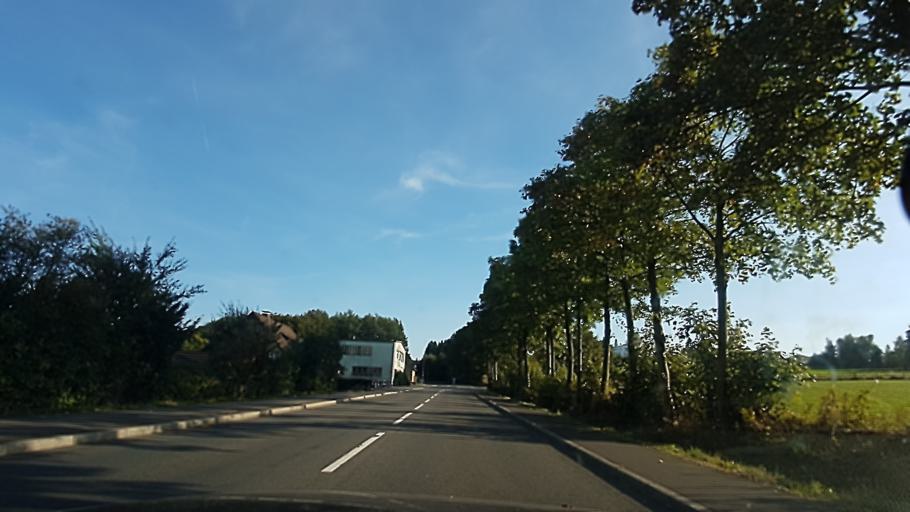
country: DE
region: North Rhine-Westphalia
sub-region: Regierungsbezirk Koln
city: Marienheide
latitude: 51.0734
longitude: 7.5560
